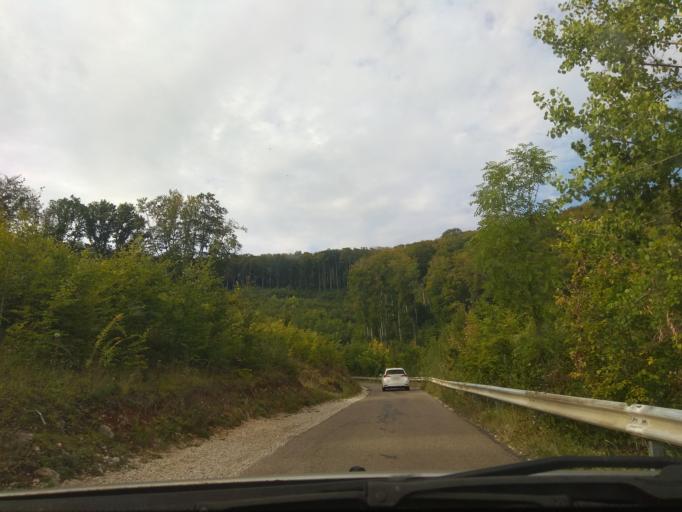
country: HU
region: Borsod-Abauj-Zemplen
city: Sajobabony
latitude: 48.0699
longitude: 20.6627
